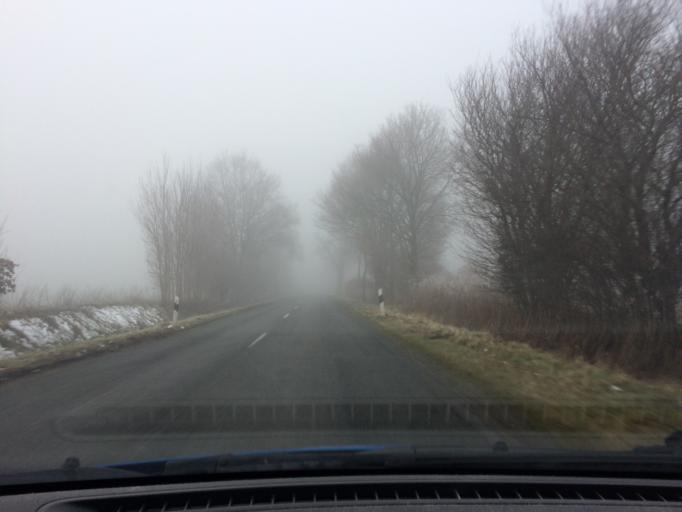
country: DE
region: Schleswig-Holstein
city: Kruzen
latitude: 53.3934
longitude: 10.5273
